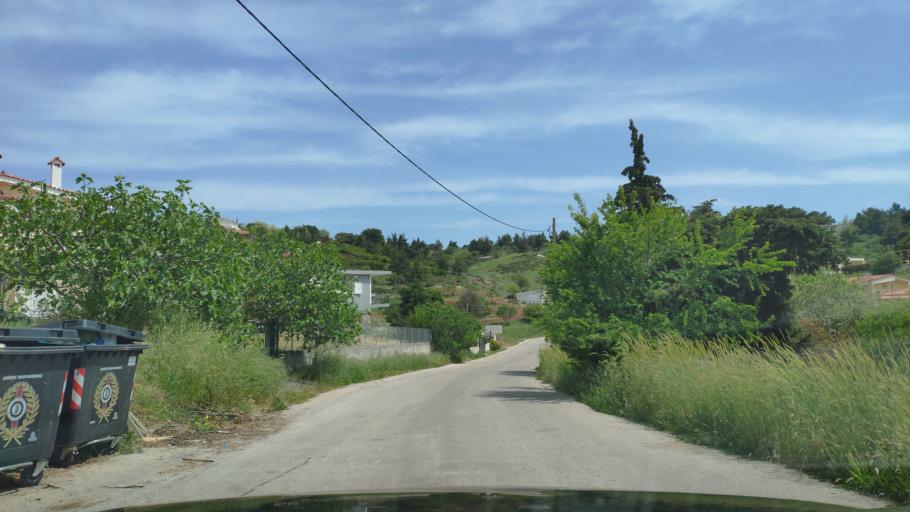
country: GR
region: Attica
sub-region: Nomarchia Anatolikis Attikis
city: Varnavas
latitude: 38.2251
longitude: 23.9252
